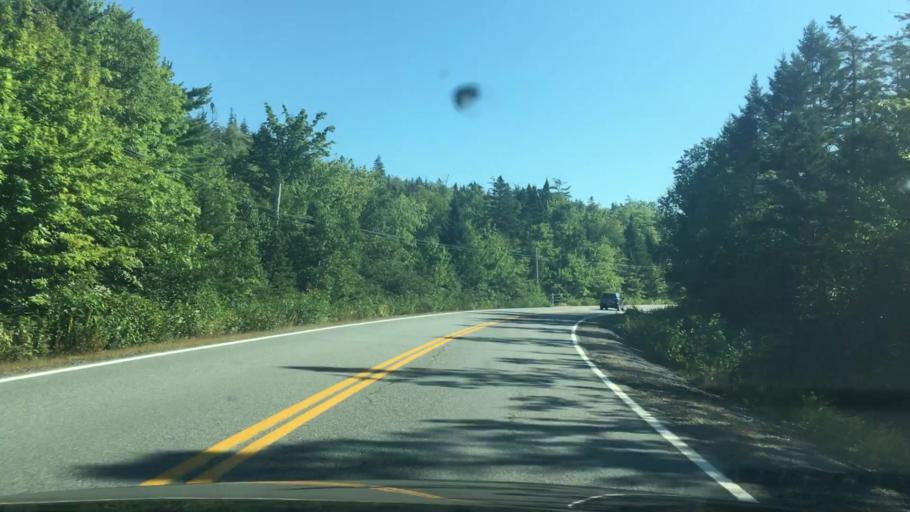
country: CA
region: Nova Scotia
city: Cole Harbour
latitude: 44.8164
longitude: -62.8833
